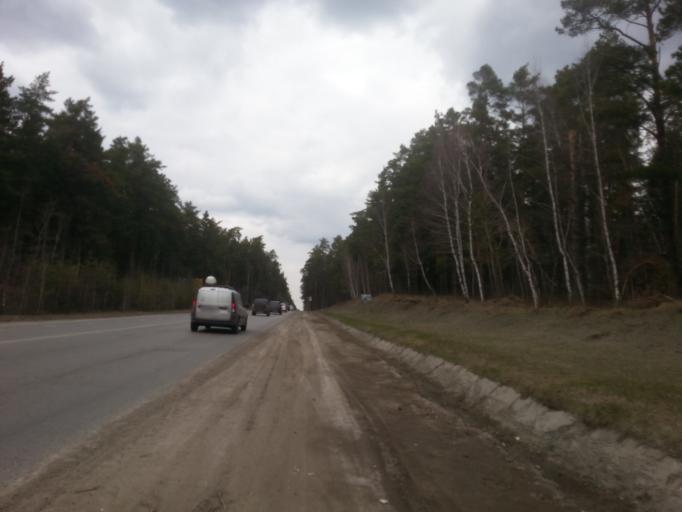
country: RU
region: Altai Krai
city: Yuzhnyy
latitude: 53.2701
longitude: 83.7251
